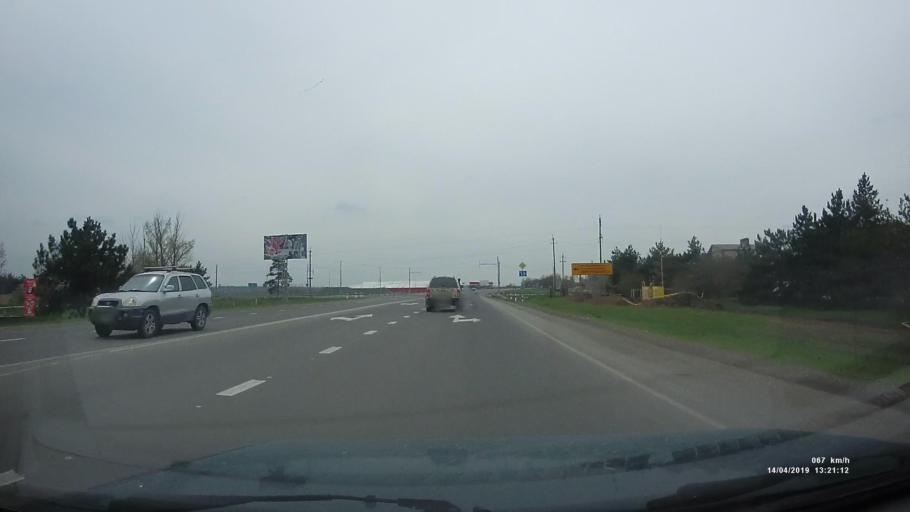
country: RU
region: Rostov
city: Kuleshovka
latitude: 47.0818
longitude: 39.5288
